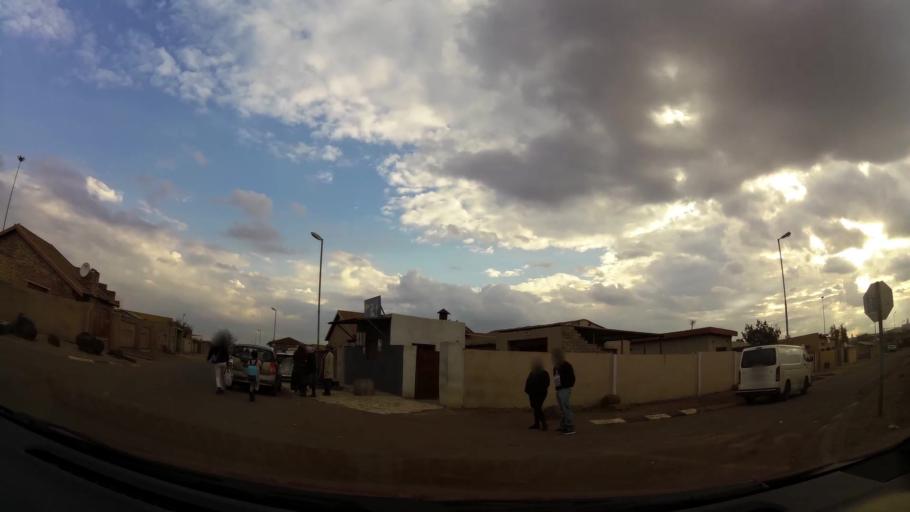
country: ZA
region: Gauteng
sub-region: City of Johannesburg Metropolitan Municipality
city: Soweto
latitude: -26.2419
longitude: 27.8214
